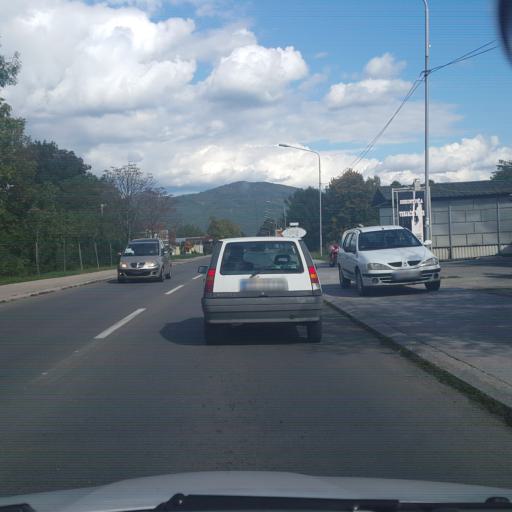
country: RS
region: Central Serbia
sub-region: Raski Okrug
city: Vrnjacka Banja
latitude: 43.6335
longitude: 20.9070
